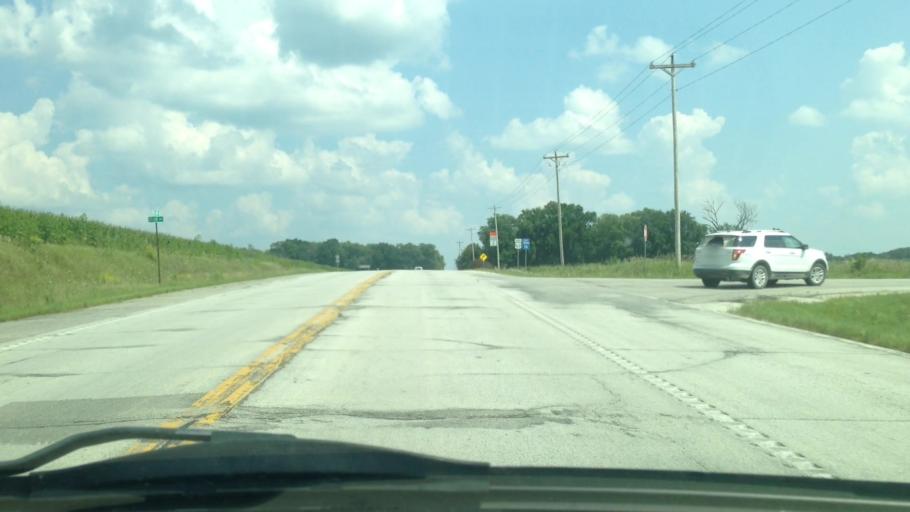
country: US
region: Minnesota
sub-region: Fillmore County
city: Spring Valley
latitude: 43.7110
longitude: -92.4283
